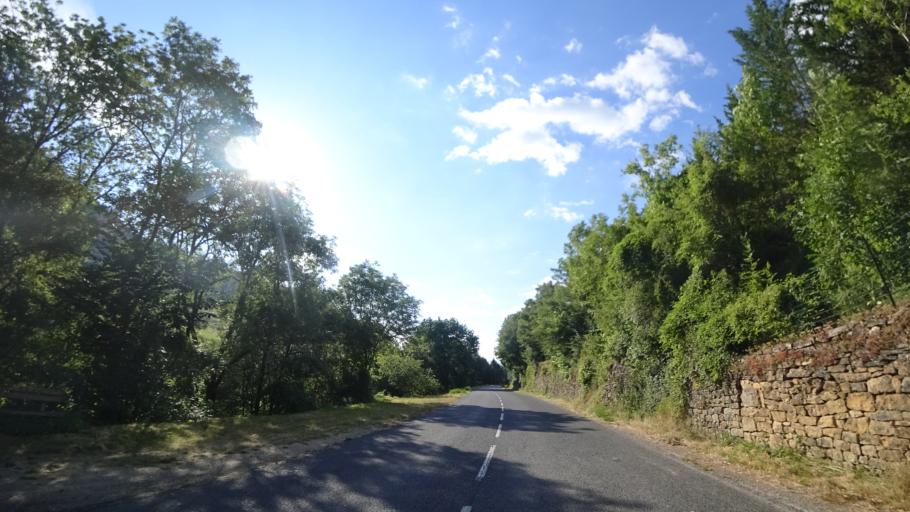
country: FR
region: Languedoc-Roussillon
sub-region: Departement de la Lozere
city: La Canourgue
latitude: 44.4185
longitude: 3.2301
